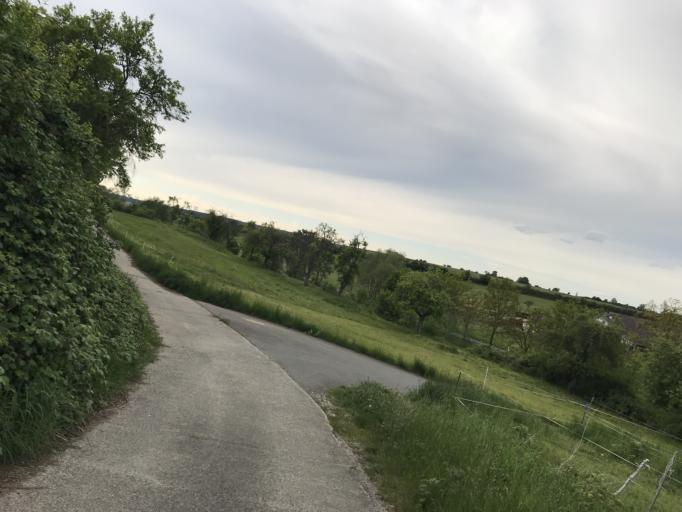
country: DE
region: Hesse
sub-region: Regierungsbezirk Giessen
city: Hoernsheim
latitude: 50.5141
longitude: 8.6144
